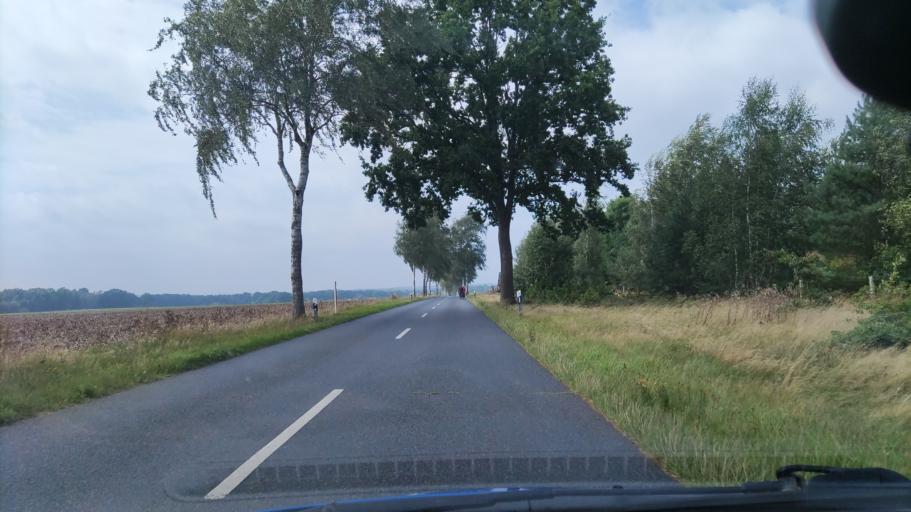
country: DE
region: Lower Saxony
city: Bienenbuttel
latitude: 53.1449
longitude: 10.5258
